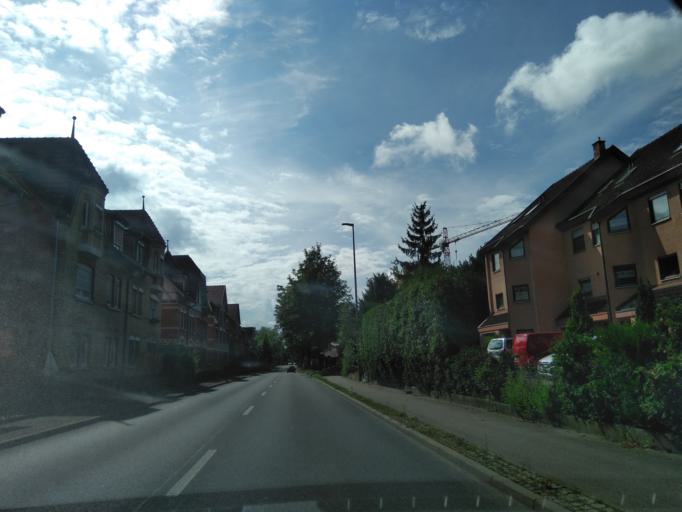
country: DE
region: Baden-Wuerttemberg
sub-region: Regierungsbezirk Stuttgart
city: Besigheim
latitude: 48.9728
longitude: 9.1433
